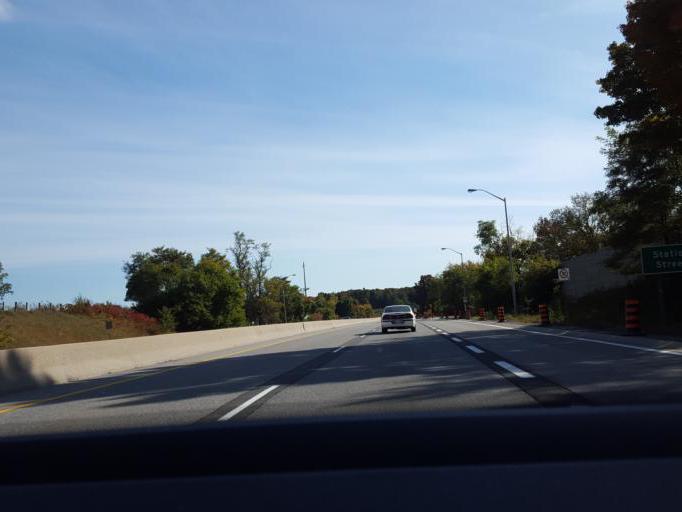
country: CA
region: Ontario
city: Oshawa
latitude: 43.9752
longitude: -78.6110
